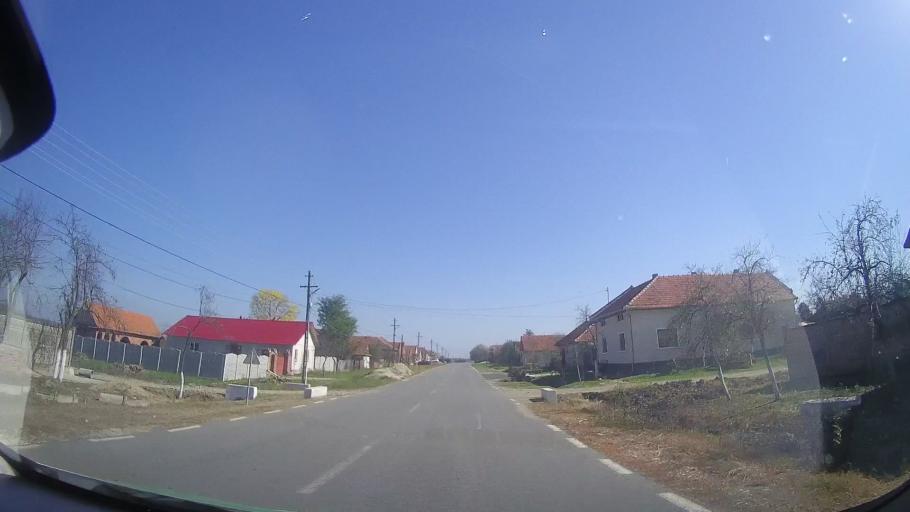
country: RO
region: Timis
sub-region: Comuna Bethausen
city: Bethausen
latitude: 45.7939
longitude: 21.9674
